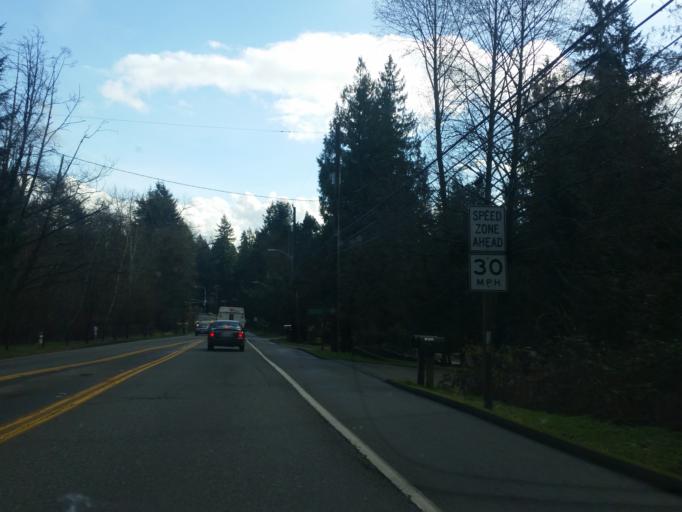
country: US
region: Washington
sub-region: King County
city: Lake Forest Park
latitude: 47.7650
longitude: -122.2951
